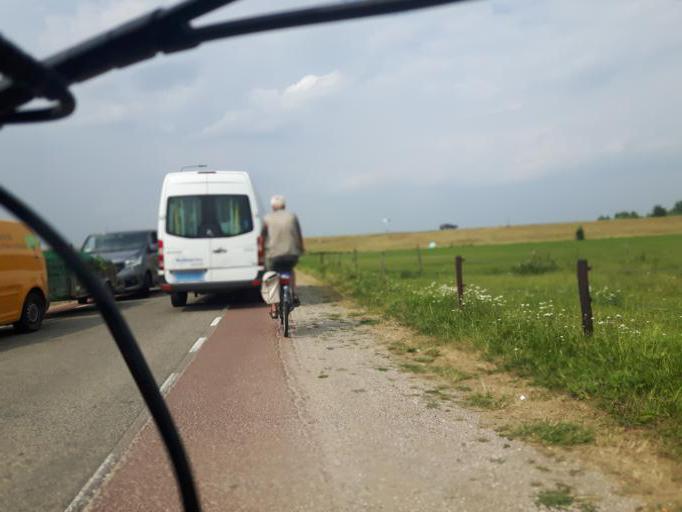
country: NL
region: South Holland
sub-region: Gemeente Leerdam
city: Leerdam
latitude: 51.8285
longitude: 5.0931
